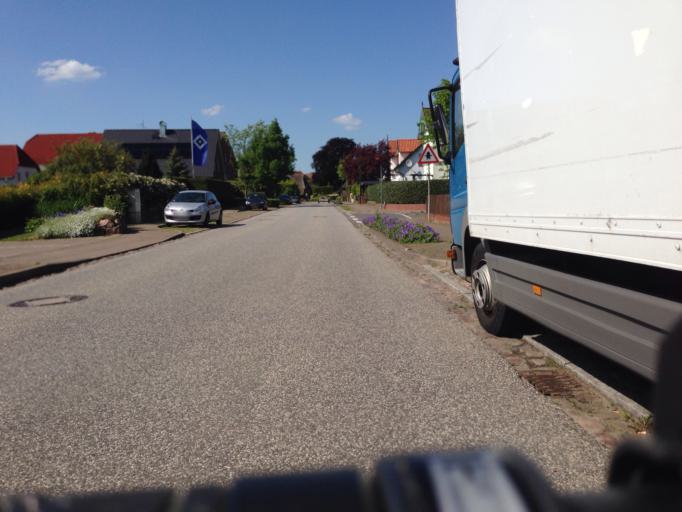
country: DE
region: Schleswig-Holstein
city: Stapelfeld
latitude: 53.6032
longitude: 10.2222
